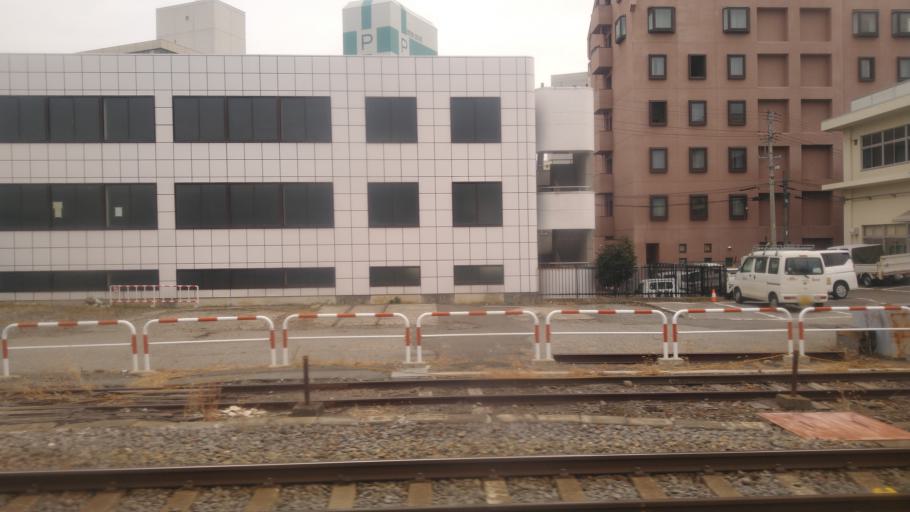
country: JP
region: Nagano
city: Matsumoto
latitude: 36.2323
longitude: 137.9638
